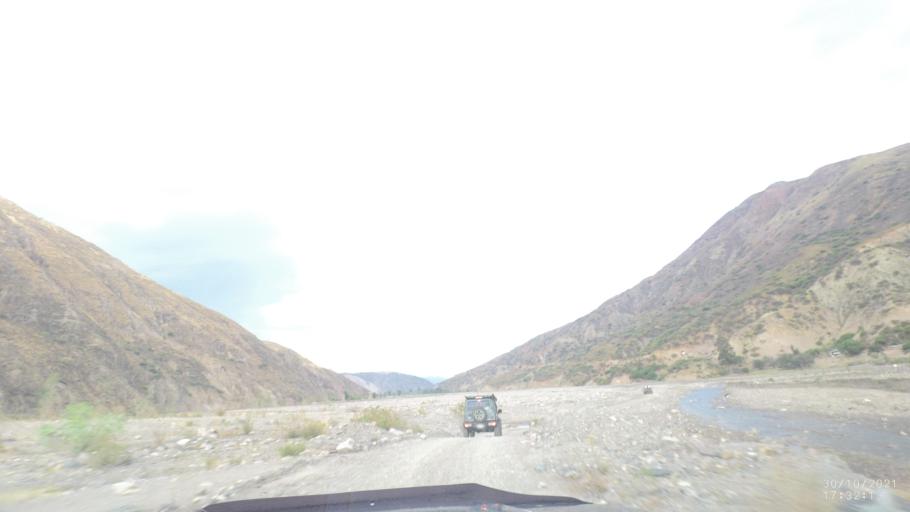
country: BO
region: Cochabamba
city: Sipe Sipe
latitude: -17.5254
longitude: -66.5872
